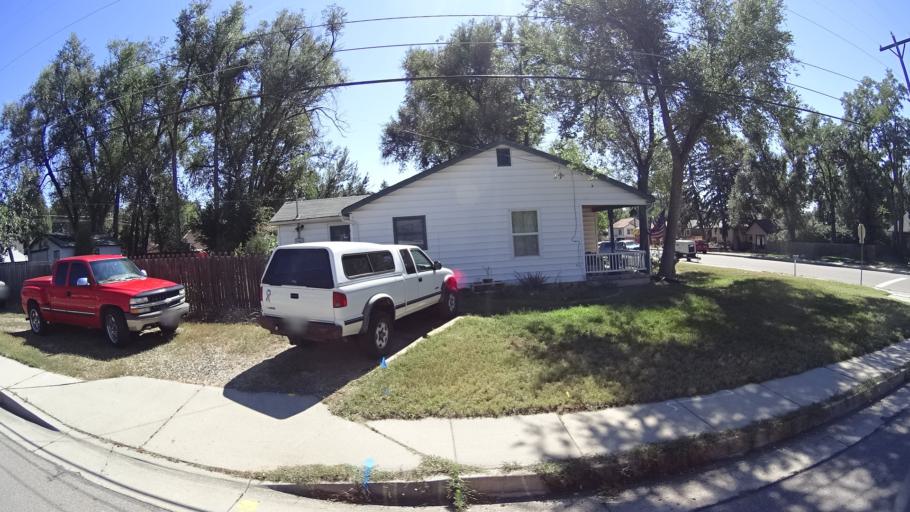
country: US
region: Colorado
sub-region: El Paso County
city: Colorado Springs
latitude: 38.8433
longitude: -104.8463
